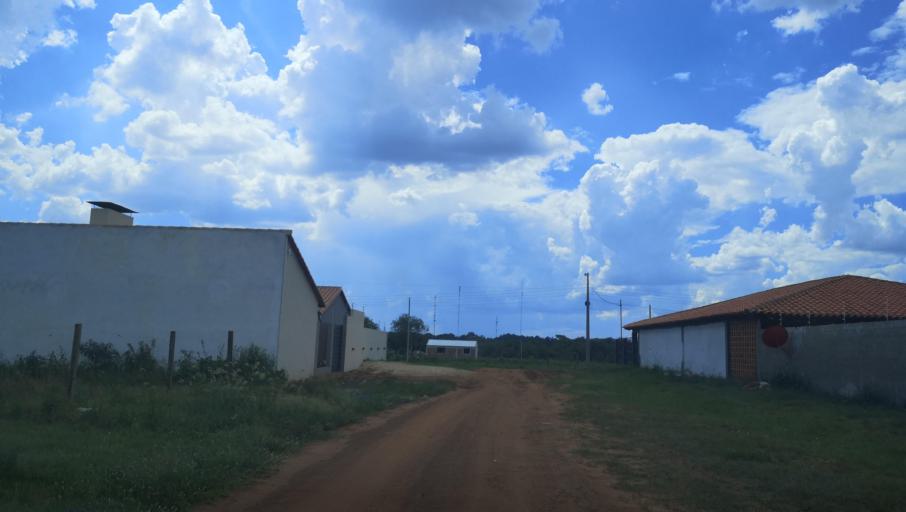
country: PY
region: Misiones
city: Santa Maria
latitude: -26.8966
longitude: -57.0409
